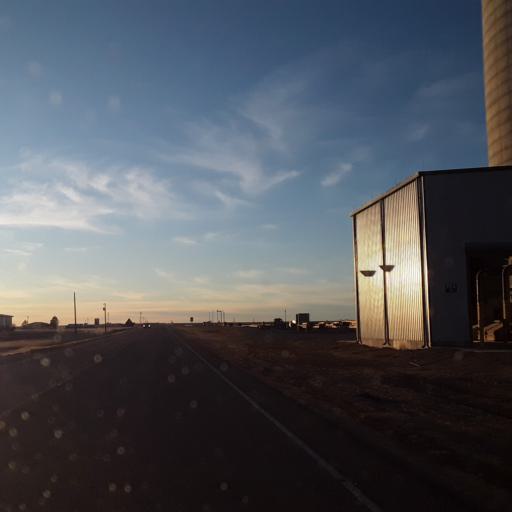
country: US
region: Colorado
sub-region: Cheyenne County
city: Cheyenne Wells
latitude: 38.8161
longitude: -102.3627
